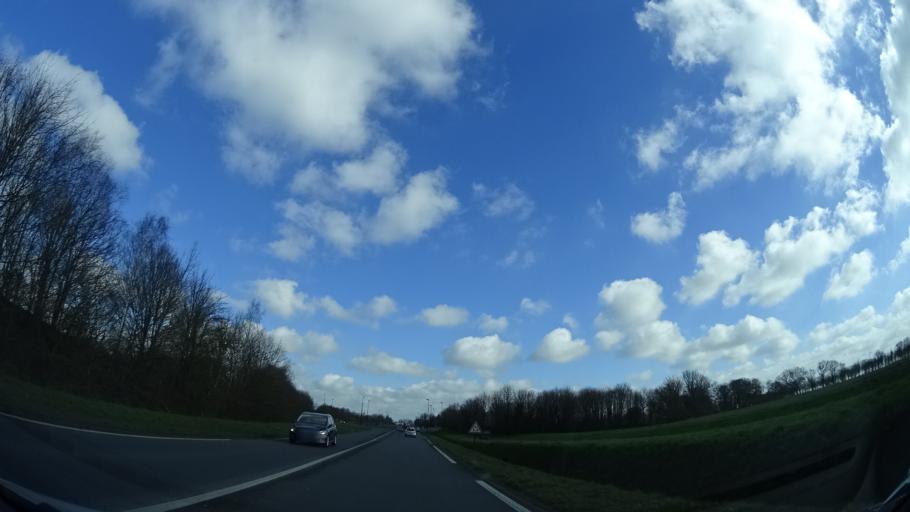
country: FR
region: Brittany
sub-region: Departement d'Ille-et-Vilaine
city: Pace
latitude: 48.1465
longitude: -1.7584
